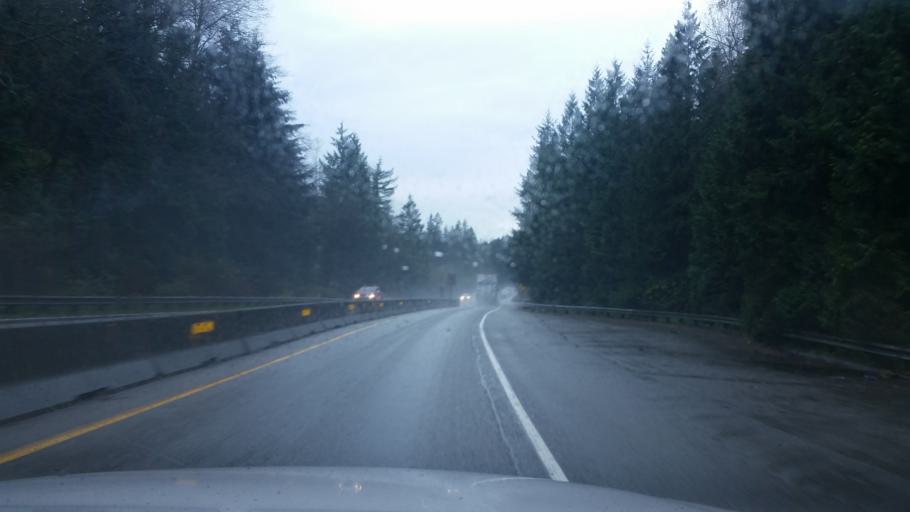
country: US
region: Washington
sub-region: King County
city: Hobart
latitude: 47.4534
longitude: -121.9521
